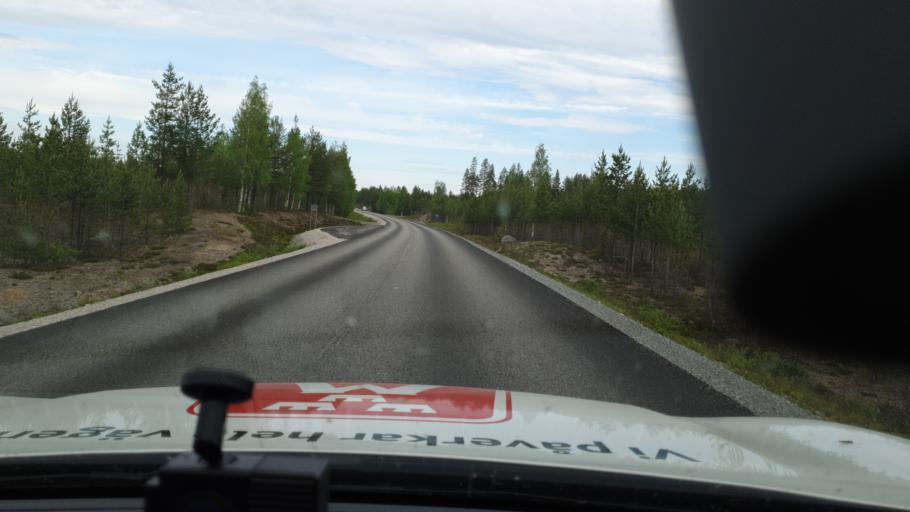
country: SE
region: Vaesterbotten
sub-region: Mala Kommun
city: Mala
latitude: 64.9678
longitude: 18.5805
